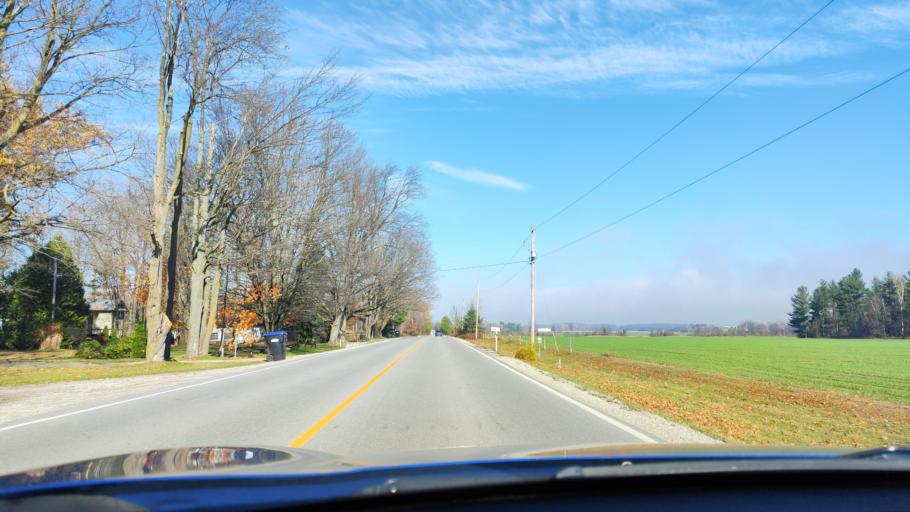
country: CA
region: Ontario
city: Wasaga Beach
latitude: 44.4117
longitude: -80.0604
